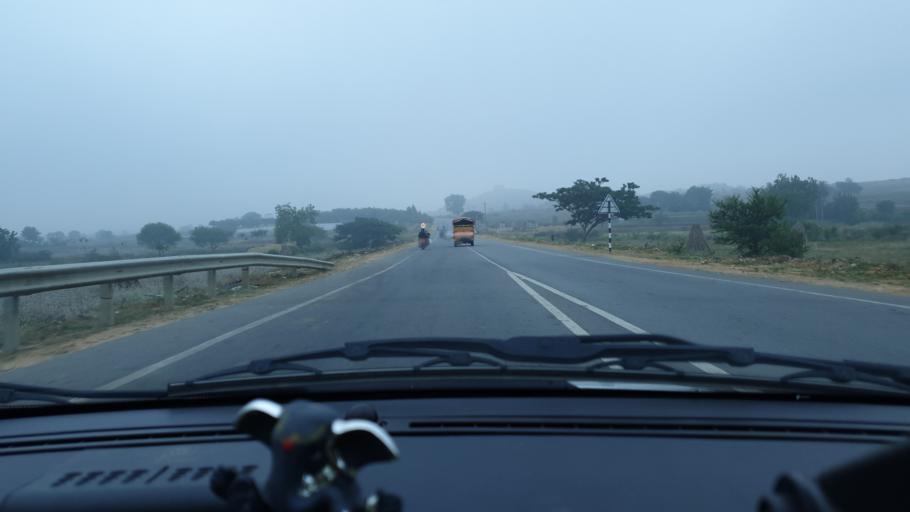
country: IN
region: Telangana
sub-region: Mahbubnagar
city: Farrukhnagar
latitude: 16.9488
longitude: 78.5236
